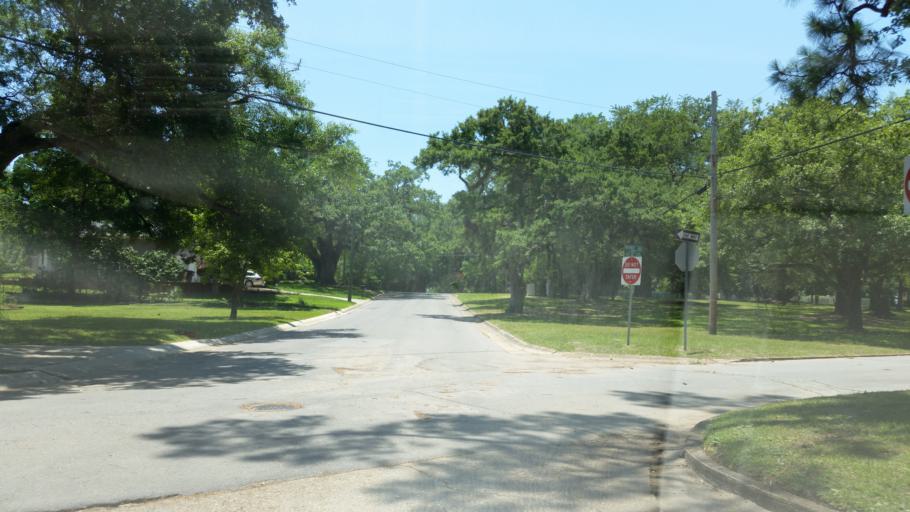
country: US
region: Florida
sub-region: Escambia County
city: Pensacola
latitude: 30.4328
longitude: -87.2078
